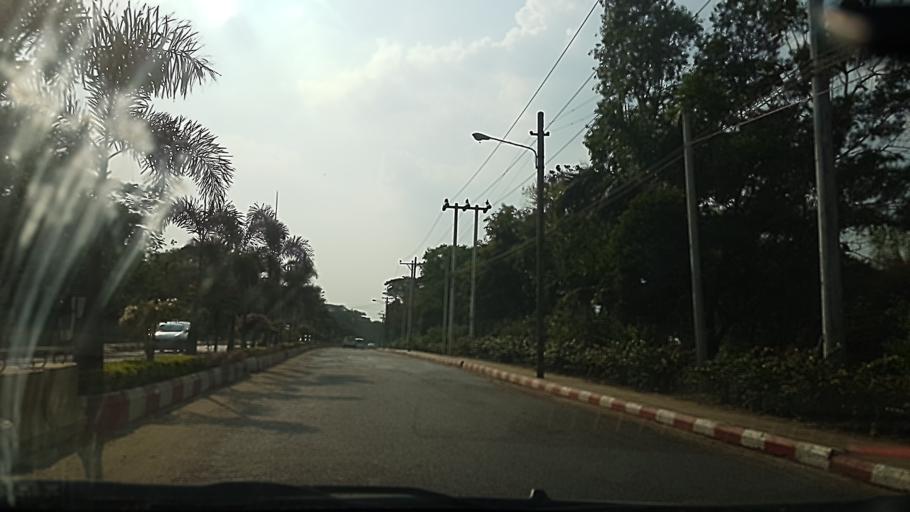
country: MM
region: Yangon
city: Syriam
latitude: 16.7787
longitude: 96.2457
